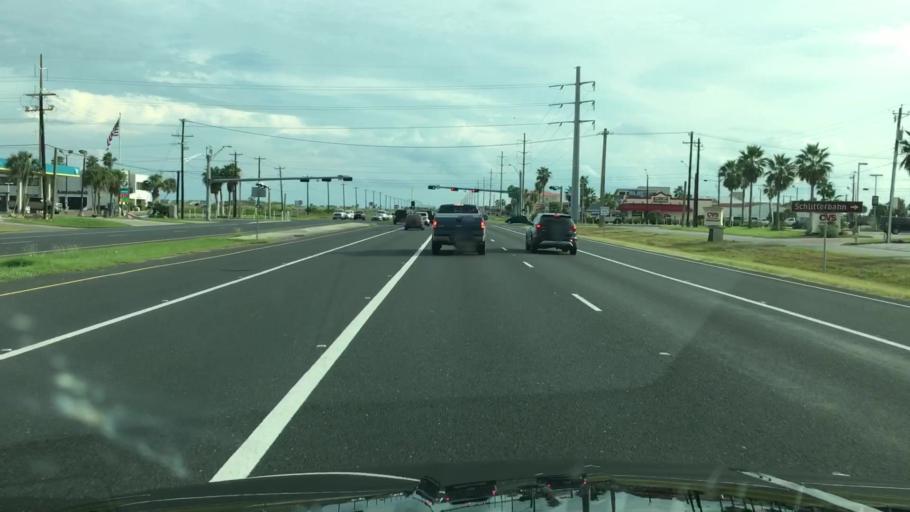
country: US
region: Texas
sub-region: Nueces County
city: Corpus Christi
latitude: 27.6192
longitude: -97.2218
